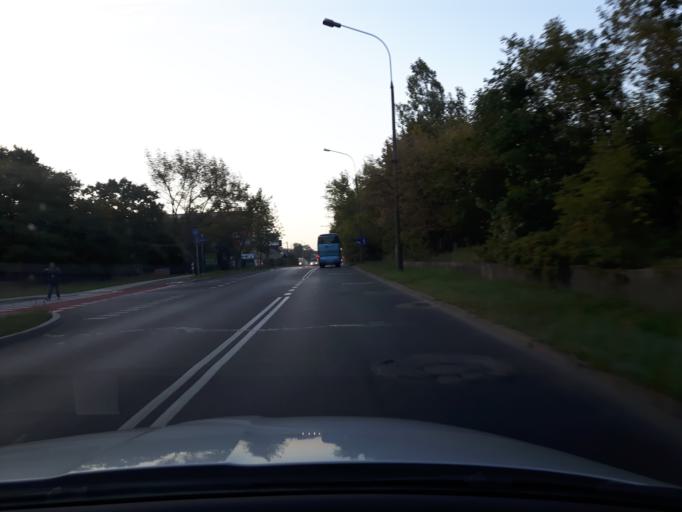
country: PL
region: Masovian Voivodeship
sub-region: Warszawa
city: Wawer
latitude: 52.2083
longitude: 21.1652
